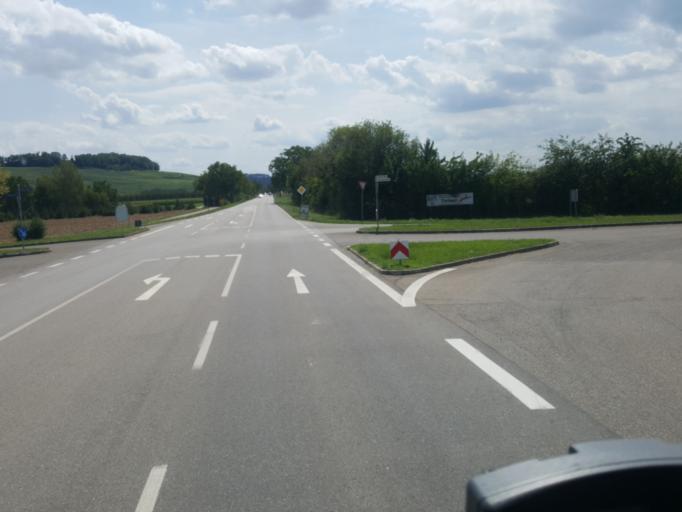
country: DE
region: Baden-Wuerttemberg
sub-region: Freiburg Region
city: Auggen
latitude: 47.7858
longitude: 7.5891
